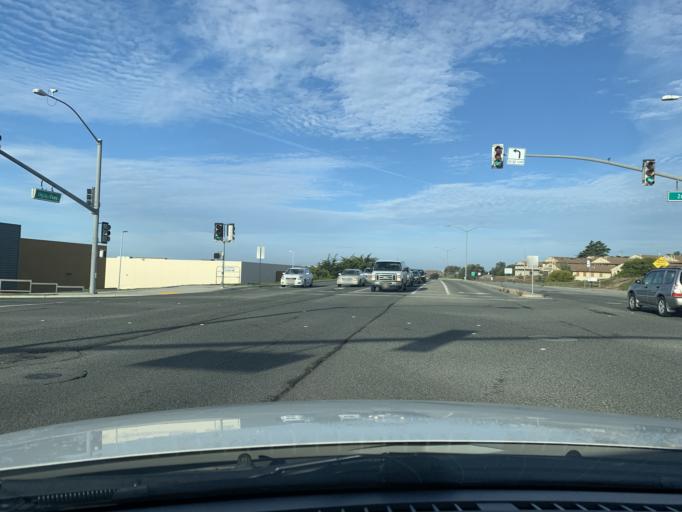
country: US
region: California
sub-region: Monterey County
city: Marina
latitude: 36.6678
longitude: -121.8086
